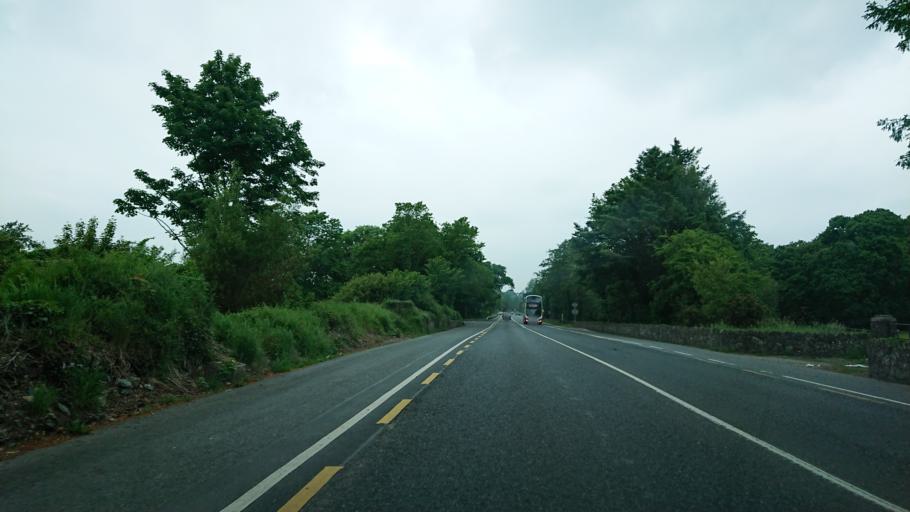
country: IE
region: Munster
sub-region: Waterford
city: Waterford
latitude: 52.2183
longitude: -7.1267
